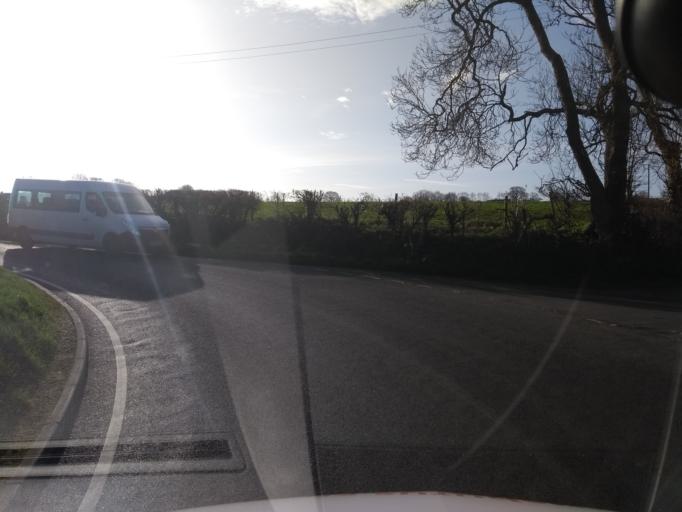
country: GB
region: England
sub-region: Somerset
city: Street
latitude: 51.1354
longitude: -2.8328
